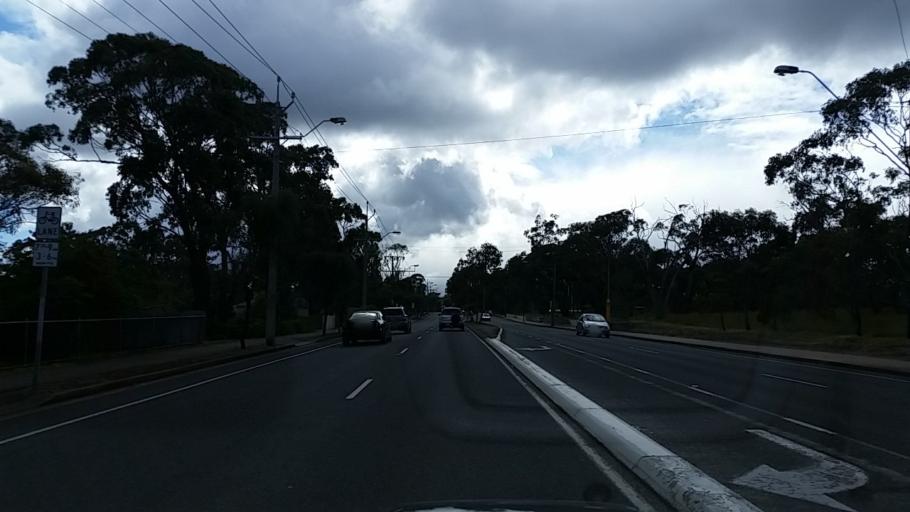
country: AU
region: South Australia
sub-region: Mitcham
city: Blackwood
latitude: -35.0277
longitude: 138.5981
